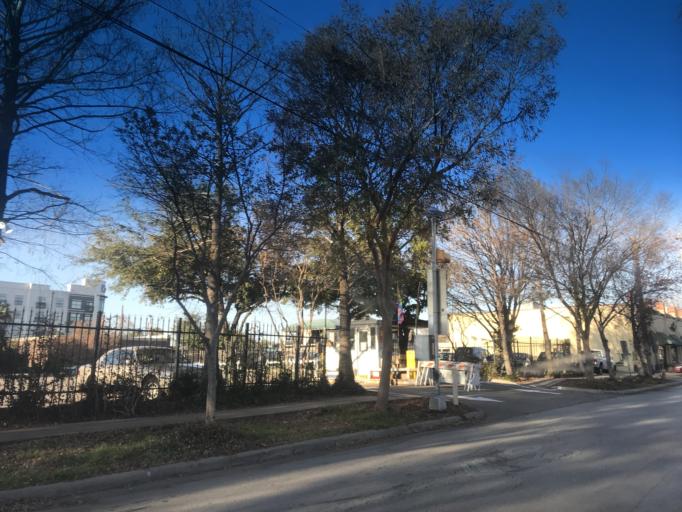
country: US
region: Texas
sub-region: Dallas County
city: Dallas
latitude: 32.8103
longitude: -96.8120
